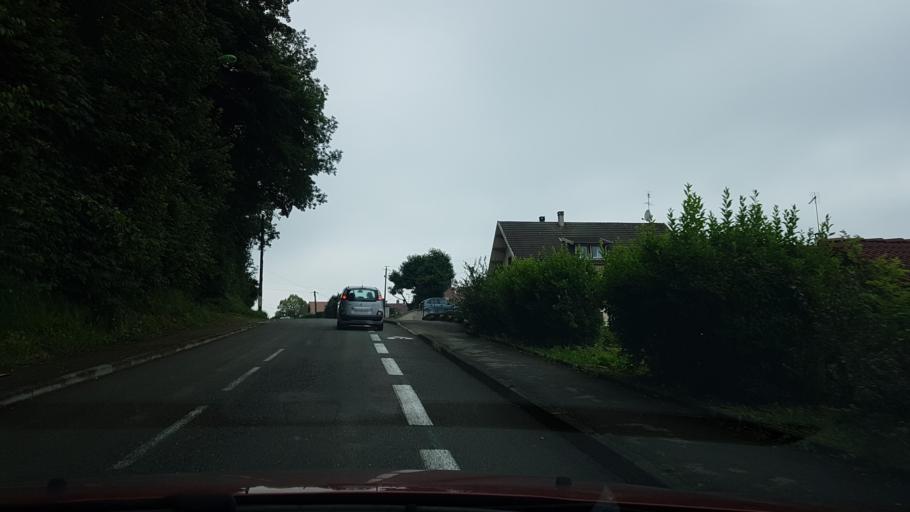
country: FR
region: Franche-Comte
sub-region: Departement du Jura
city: Montmorot
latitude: 46.6713
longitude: 5.5361
